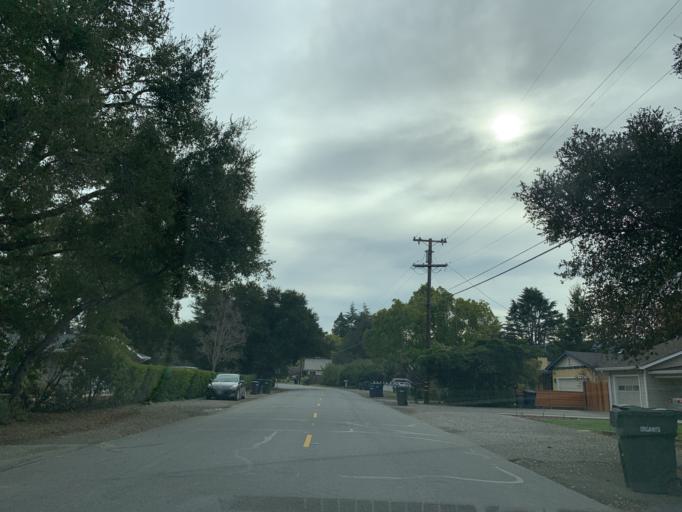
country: US
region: California
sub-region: Santa Clara County
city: Los Altos
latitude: 37.3836
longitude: -122.1001
